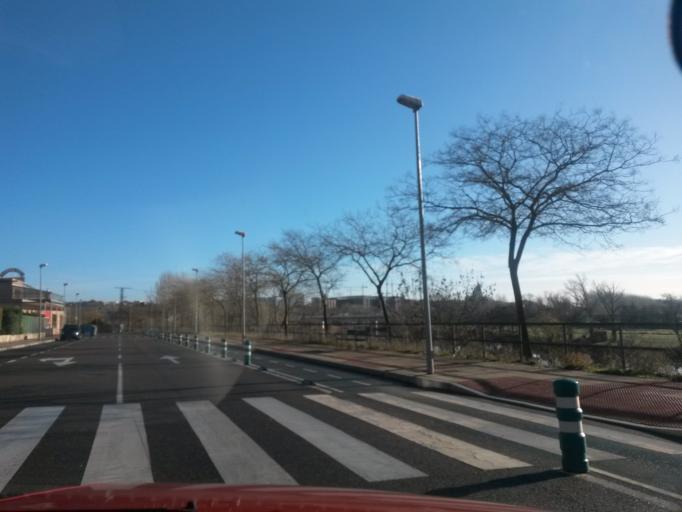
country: ES
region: Castille and Leon
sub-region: Provincia de Salamanca
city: Salamanca
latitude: 40.9629
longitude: -5.6868
